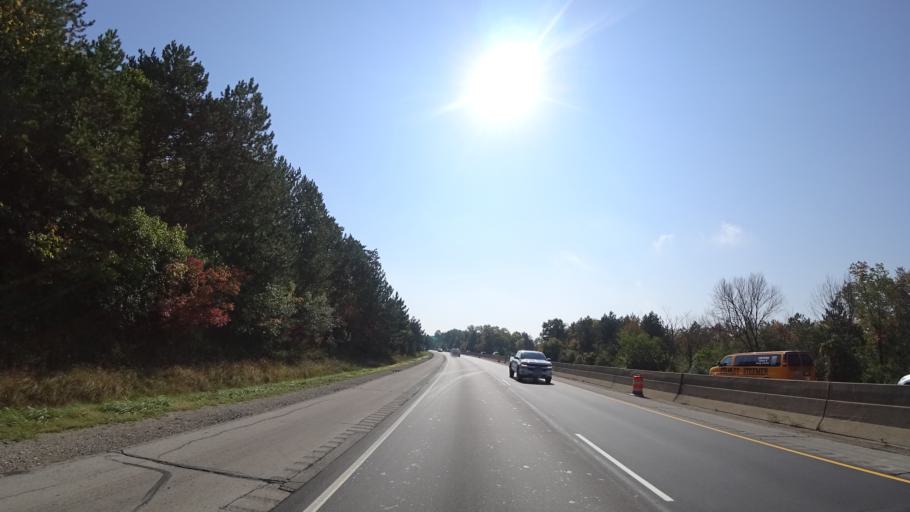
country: US
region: Michigan
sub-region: Washtenaw County
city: Ann Arbor
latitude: 42.2653
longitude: -83.7846
